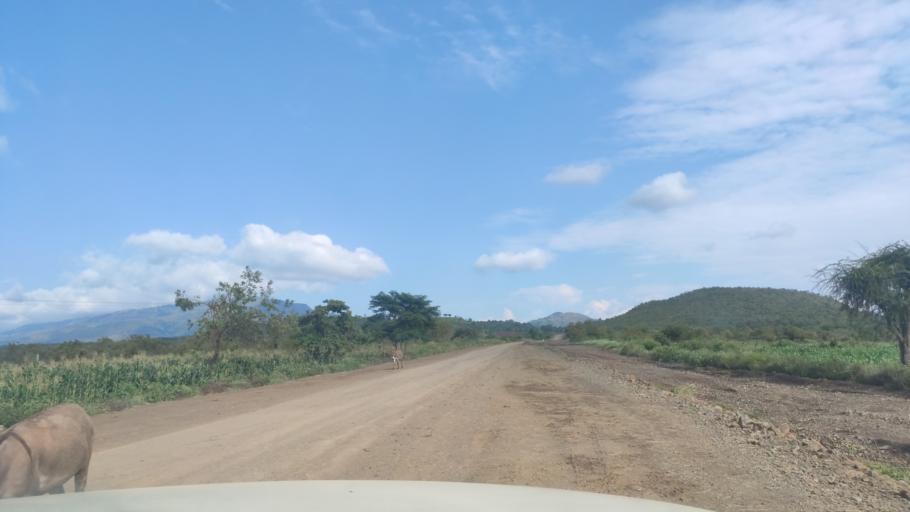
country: ET
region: Southern Nations, Nationalities, and People's Region
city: Felege Neway
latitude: 6.4341
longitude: 37.2859
